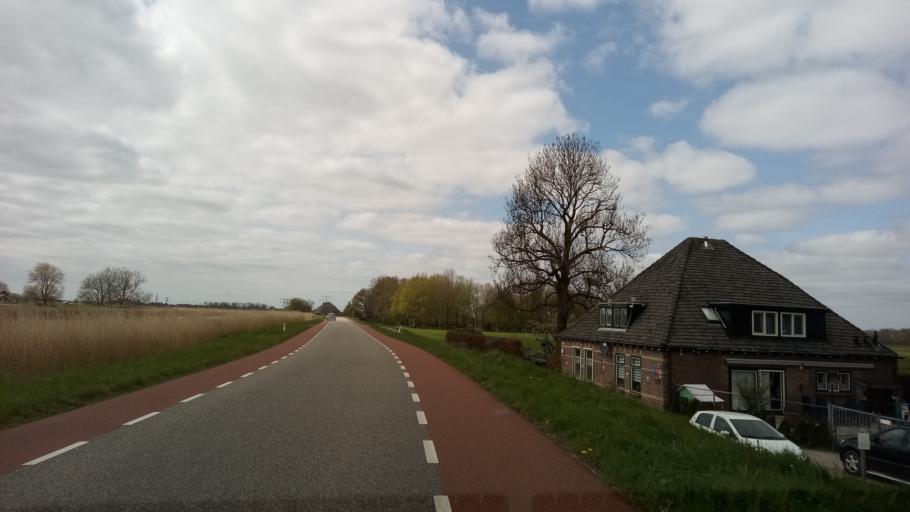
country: NL
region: North Holland
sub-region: Gemeente Heerhugowaard
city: Heerhugowaard
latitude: 52.6358
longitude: 4.8615
